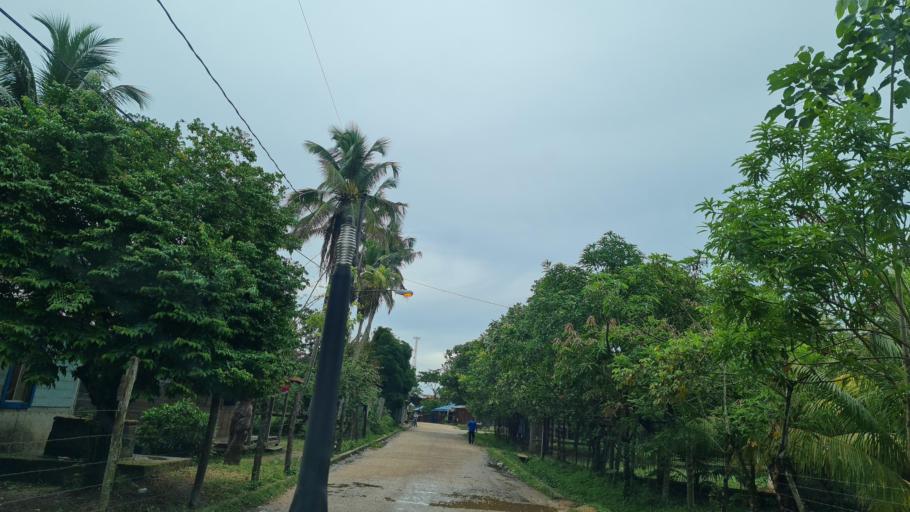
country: NI
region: Atlantico Norte (RAAN)
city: Waspam
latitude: 14.7369
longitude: -83.9699
